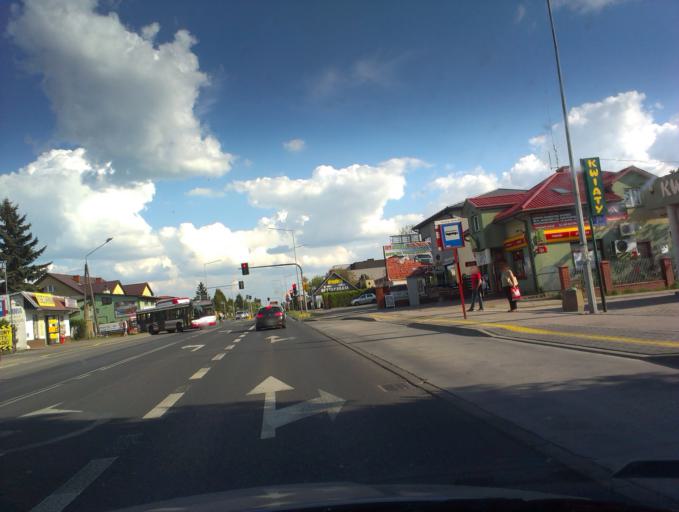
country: PL
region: Masovian Voivodeship
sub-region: Radom
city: Radom
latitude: 51.3796
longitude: 21.1827
